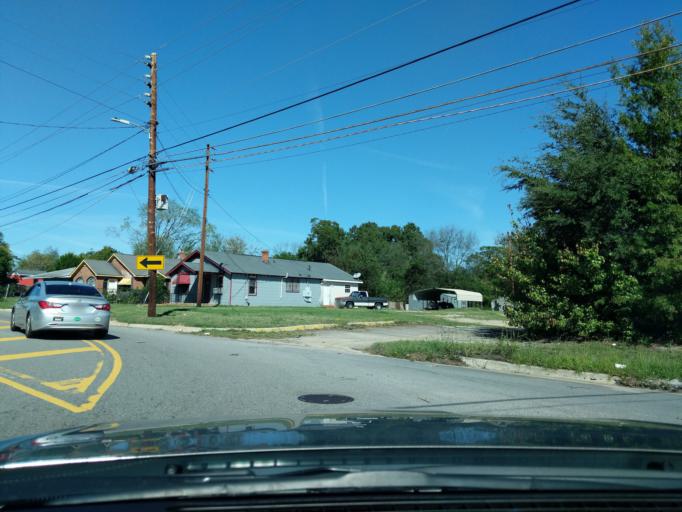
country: US
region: Georgia
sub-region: Richmond County
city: Augusta
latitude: 33.4403
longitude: -81.9991
